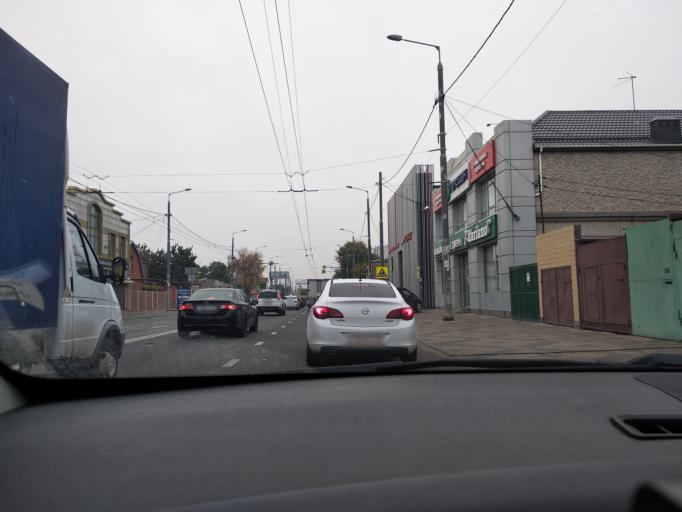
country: RU
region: Krasnodarskiy
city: Krasnodar
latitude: 45.0429
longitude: 38.9564
